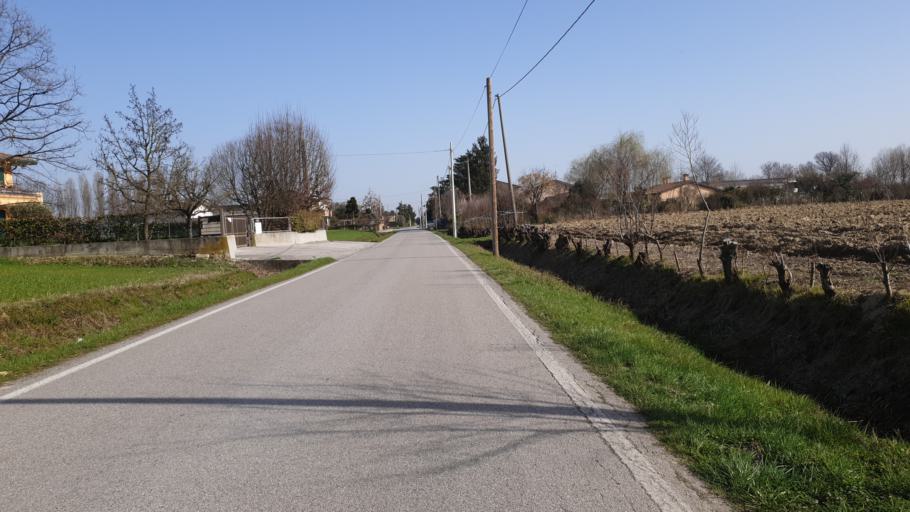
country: IT
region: Veneto
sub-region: Provincia di Padova
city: Cavino
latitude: 45.5213
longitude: 11.8720
